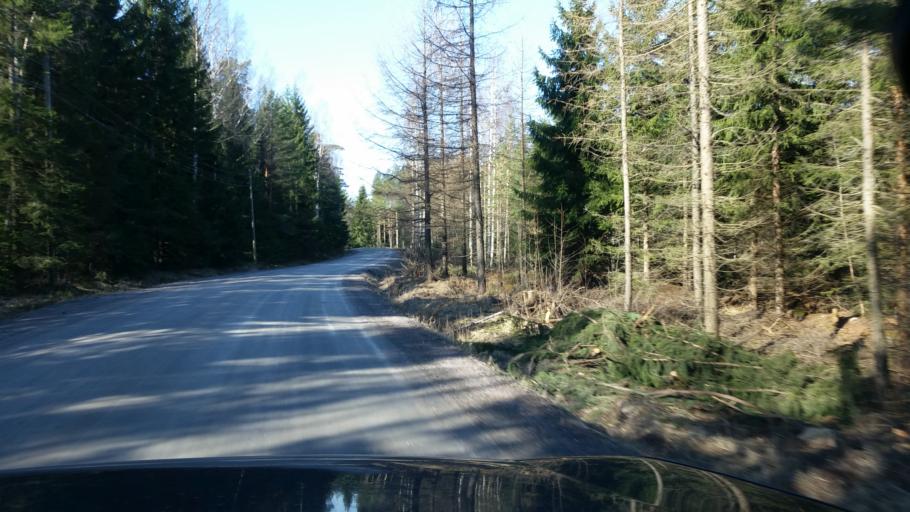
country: FI
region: Uusimaa
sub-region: Raaseporin
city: Inga
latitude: 60.0435
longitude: 23.9518
